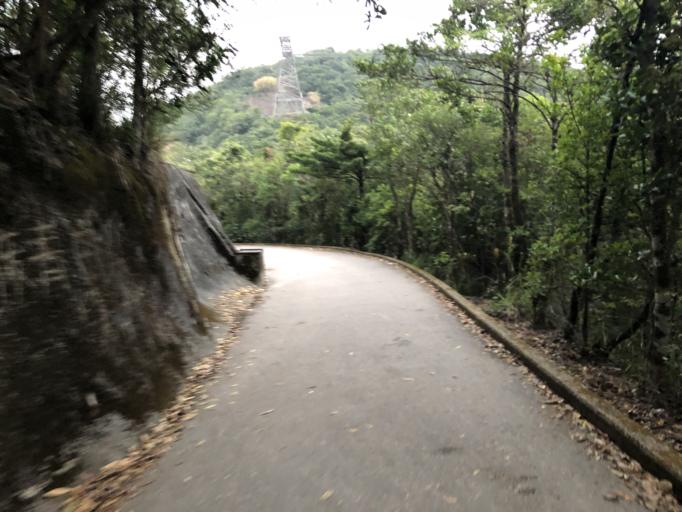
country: HK
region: Wanchai
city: Wan Chai
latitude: 22.2608
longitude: 114.2135
